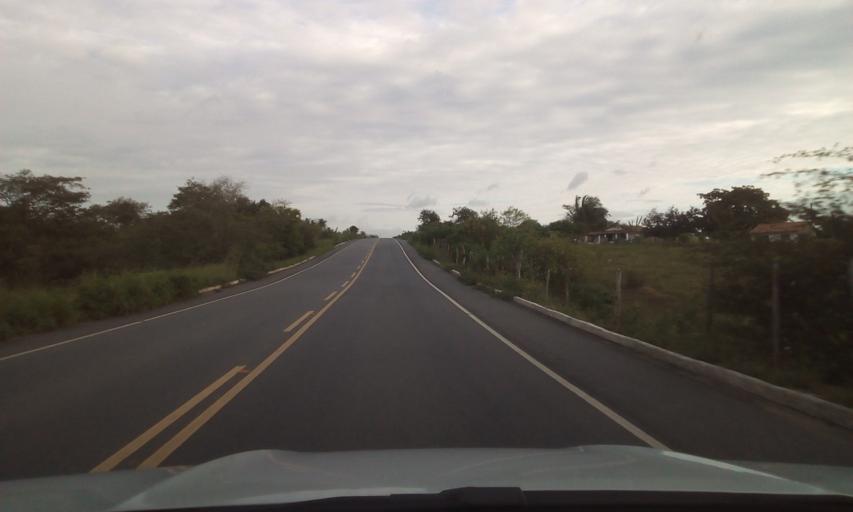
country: BR
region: Paraiba
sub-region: Serra Redonda
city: Alagoa Grande
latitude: -7.2062
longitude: -35.5917
